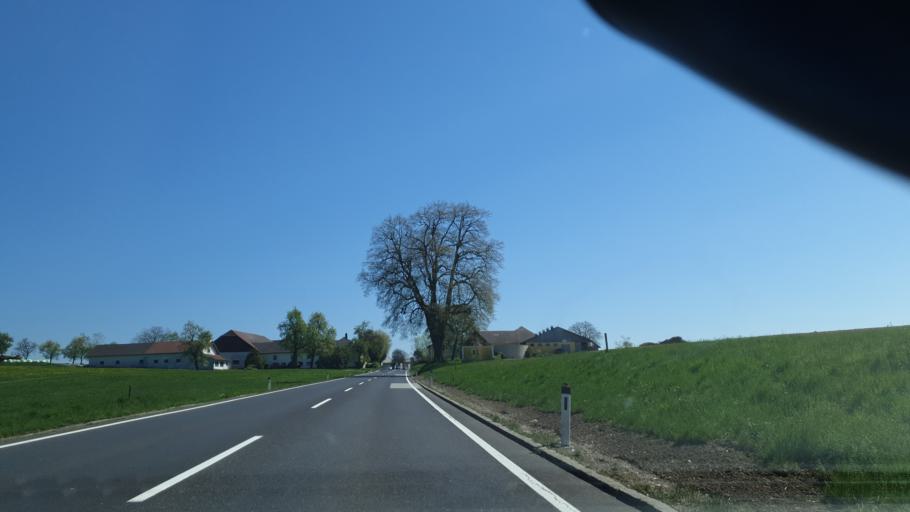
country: AT
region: Upper Austria
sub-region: Politischer Bezirk Vocklabruck
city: Gampern
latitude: 48.0011
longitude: 13.5741
